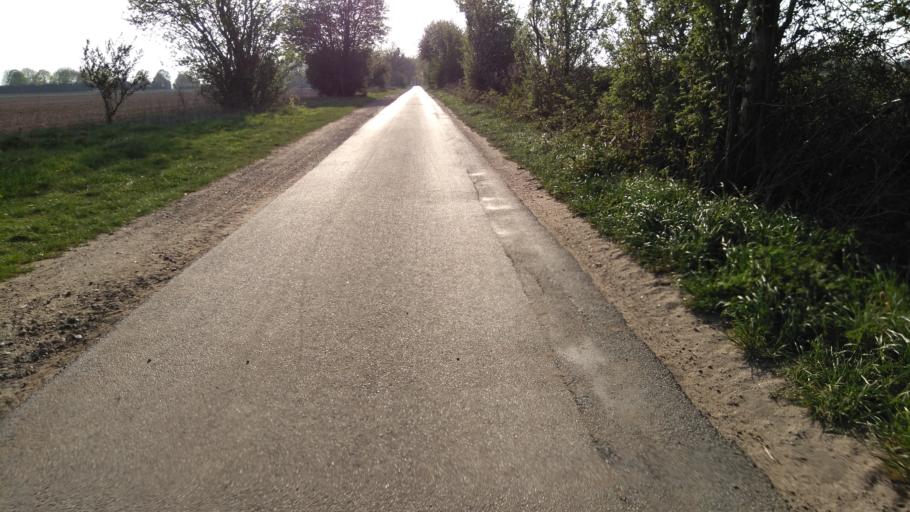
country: DE
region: Lower Saxony
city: Apensen
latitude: 53.4328
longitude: 9.6317
